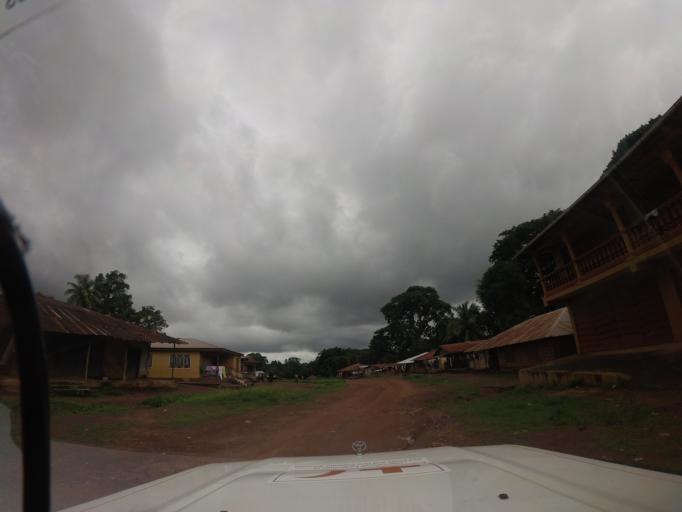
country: SL
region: Northern Province
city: Kamakwie
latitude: 9.4040
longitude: -12.2445
